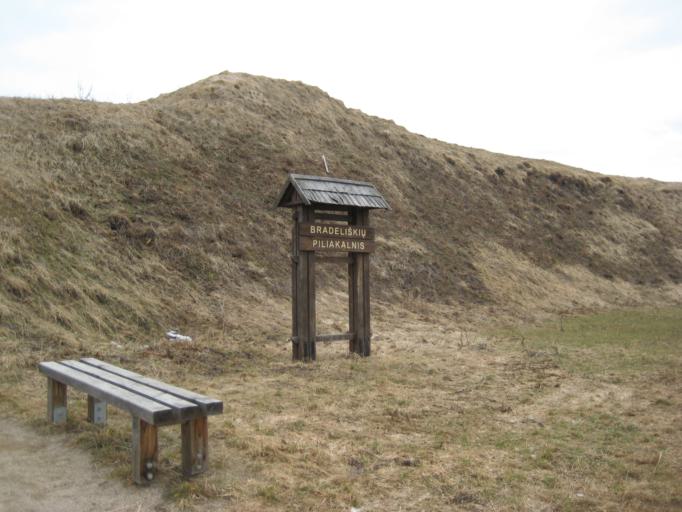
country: LT
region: Vilnius County
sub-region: Vilniaus Rajonas
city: Vievis
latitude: 54.8258
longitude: 24.9440
